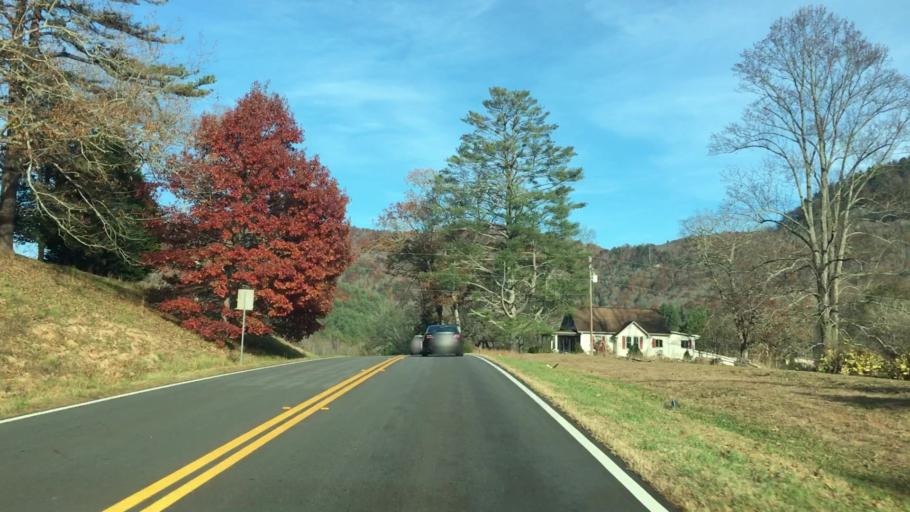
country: US
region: Georgia
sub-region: Rabun County
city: Mountain City
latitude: 34.9876
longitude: -83.3646
